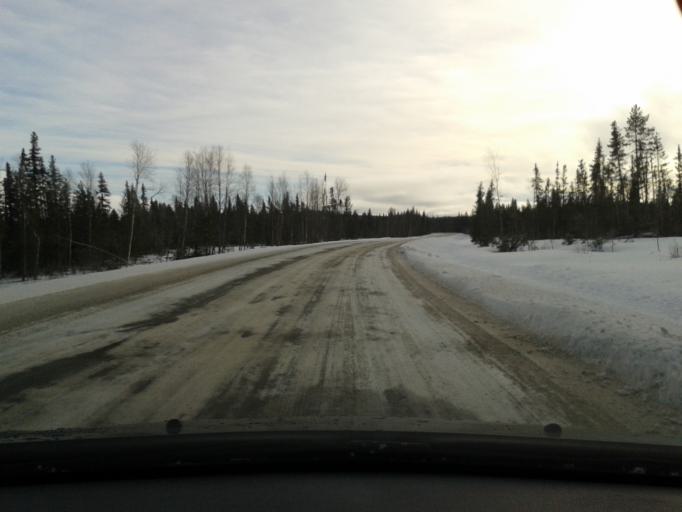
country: SE
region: Vaesterbotten
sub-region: Vilhelmina Kommun
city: Sjoberg
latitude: 64.7498
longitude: 16.1716
